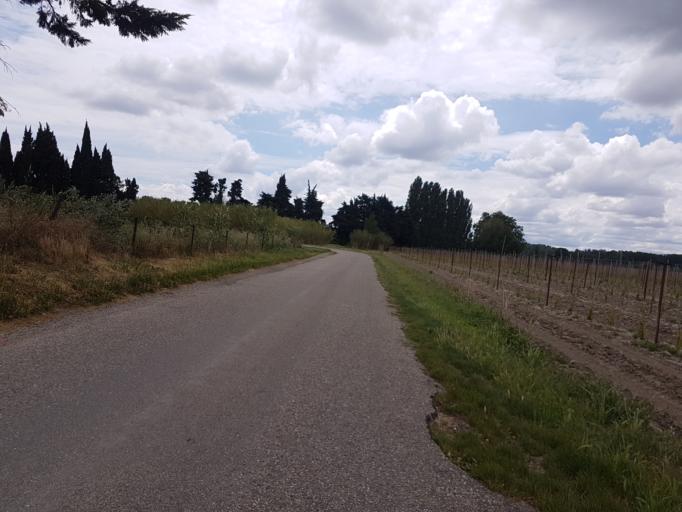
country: FR
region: Languedoc-Roussillon
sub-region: Departement du Gard
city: Vallabregues
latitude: 43.8715
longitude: 4.6229
